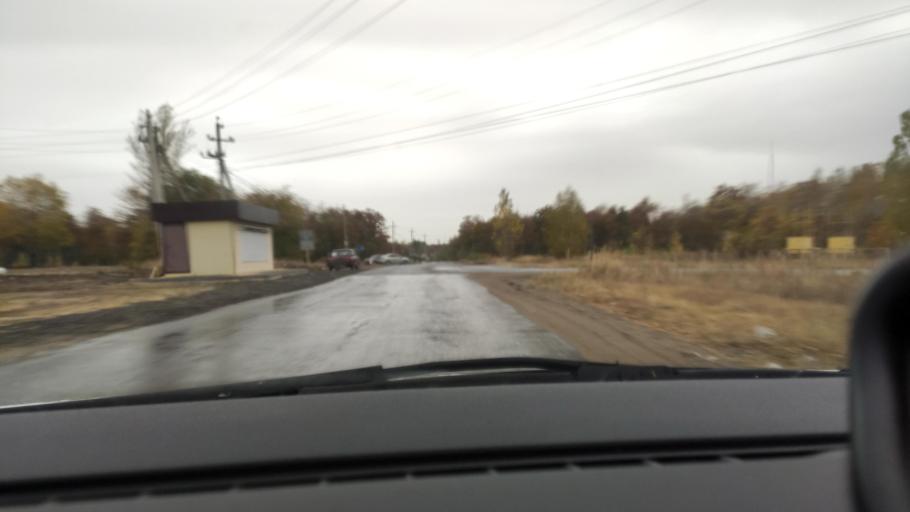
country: RU
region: Voronezj
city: Pridonskoy
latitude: 51.6404
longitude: 39.0950
